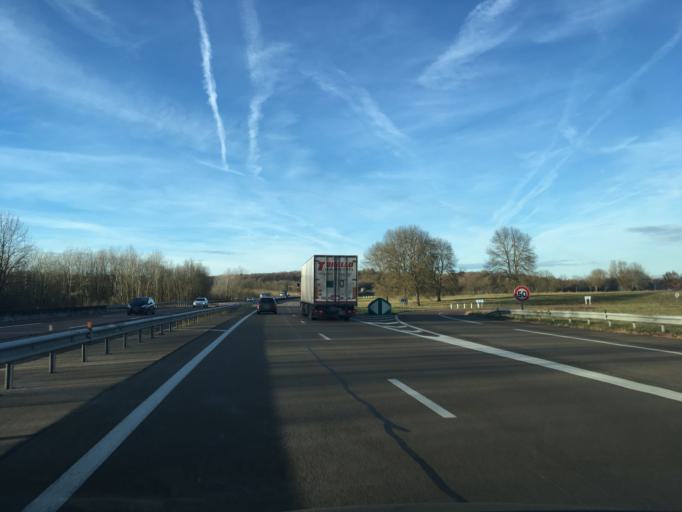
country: FR
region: Bourgogne
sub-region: Departement de l'Yonne
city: Avallon
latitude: 47.5137
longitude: 3.9943
